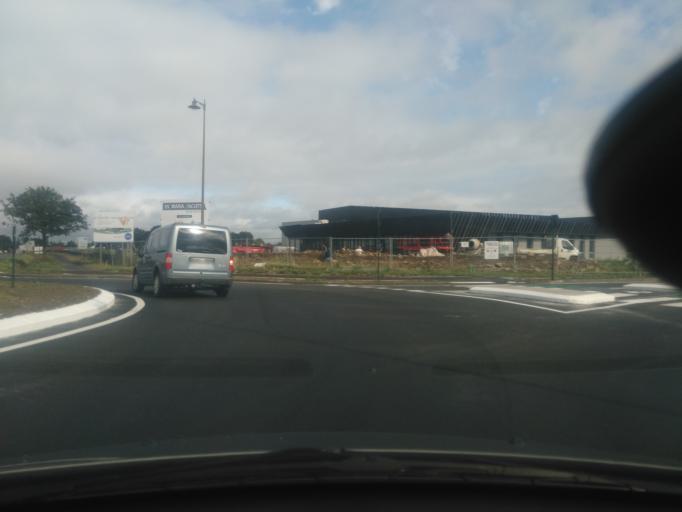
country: FR
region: Brittany
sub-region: Departement des Cotes-d'Armor
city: Lanvallay
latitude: 48.4515
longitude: -2.0152
